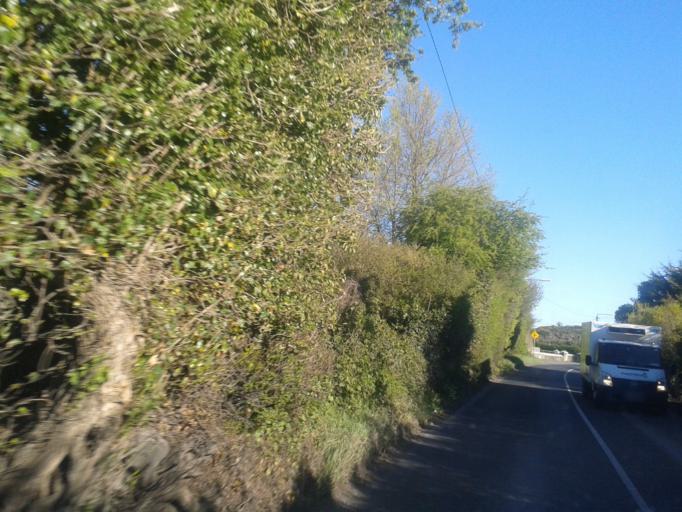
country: IE
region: Leinster
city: Kinsealy-Drinan
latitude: 53.4429
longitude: -6.1948
